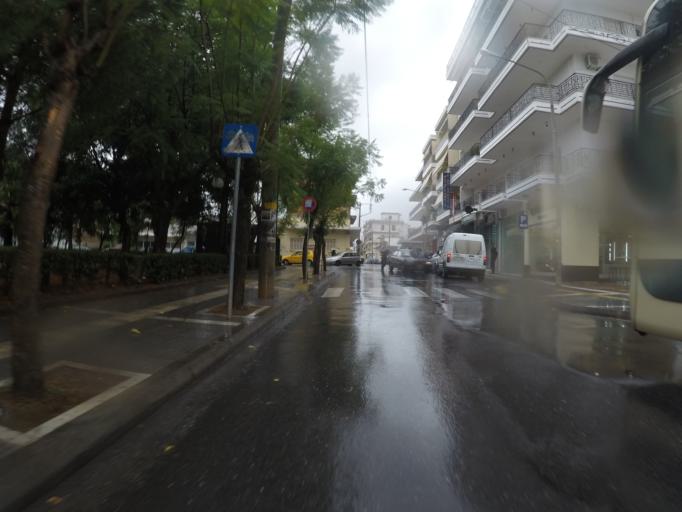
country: GR
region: Peloponnese
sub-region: Nomos Messinias
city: Messini
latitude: 37.0519
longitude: 22.0078
